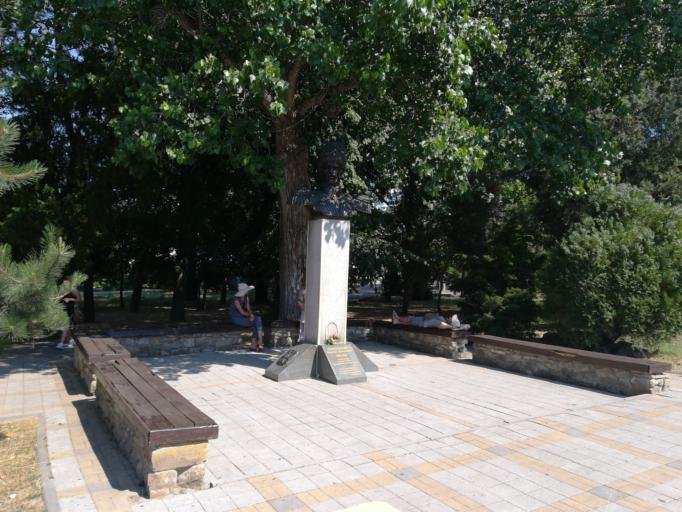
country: RU
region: Krasnodarskiy
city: Anapa
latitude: 44.8954
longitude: 37.3113
